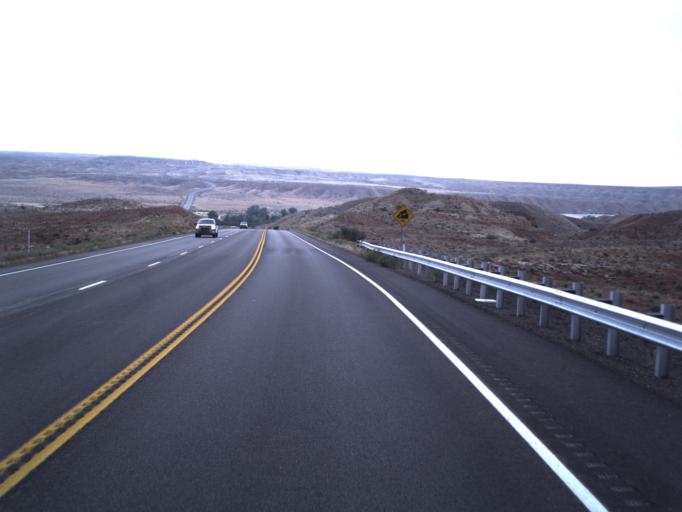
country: US
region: Utah
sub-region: Uintah County
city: Naples
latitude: 40.3244
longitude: -109.4869
